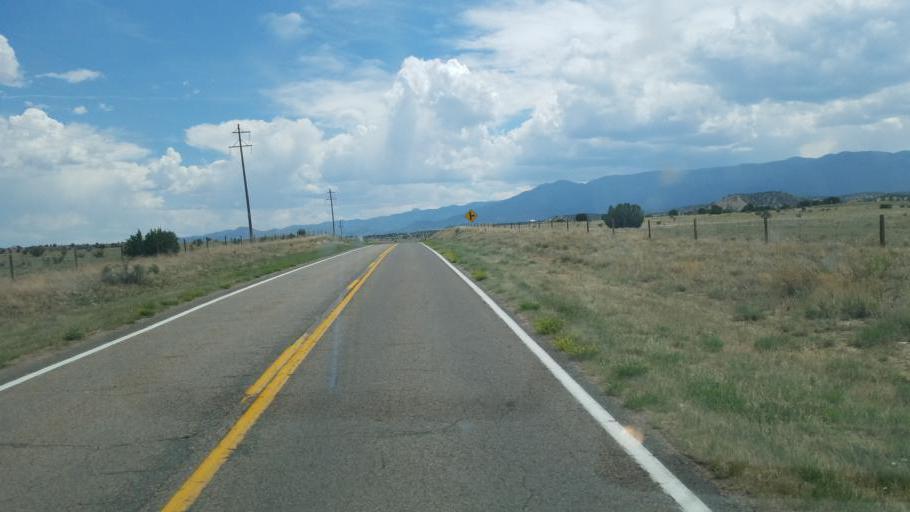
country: US
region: Colorado
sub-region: Fremont County
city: Florence
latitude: 38.3464
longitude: -105.1072
